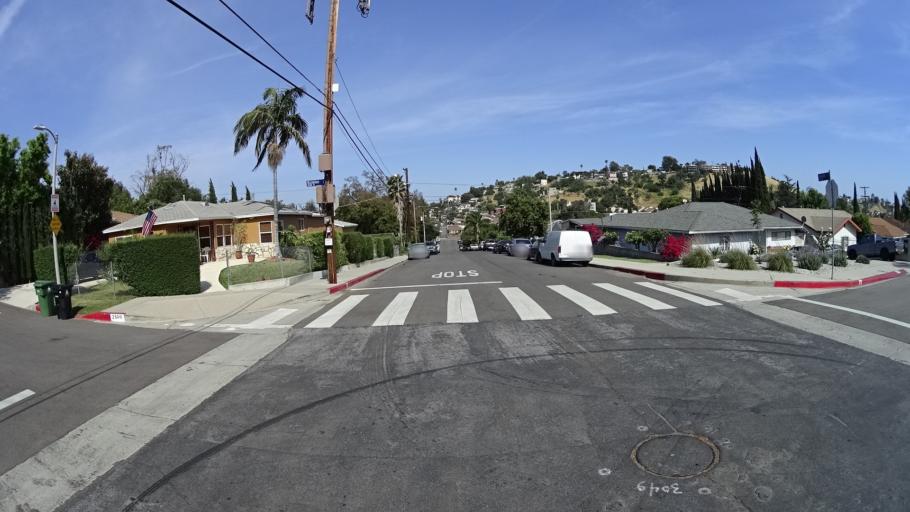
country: US
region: California
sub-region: Los Angeles County
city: Belvedere
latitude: 34.0757
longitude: -118.1830
